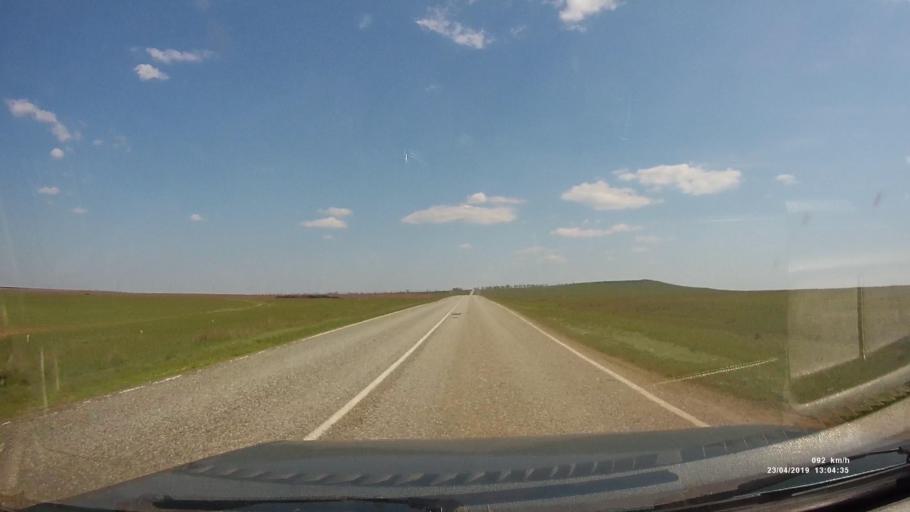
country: RU
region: Kalmykiya
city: Yashalta
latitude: 46.5934
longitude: 42.7062
